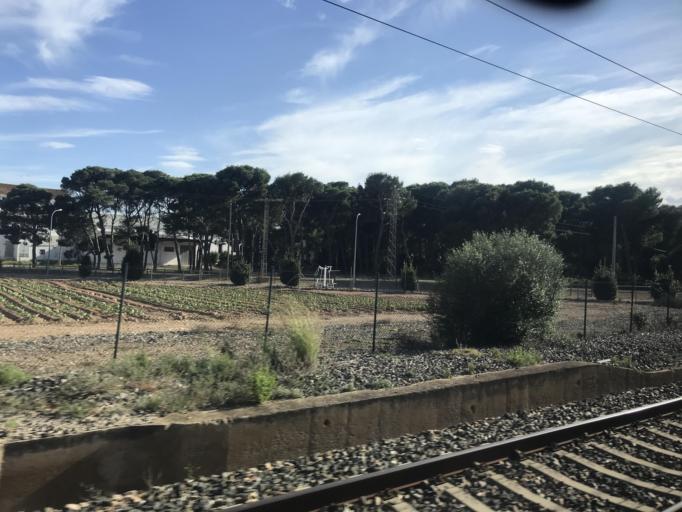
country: ES
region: Catalonia
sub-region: Provincia de Tarragona
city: Camarles
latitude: 40.7693
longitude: 0.6623
